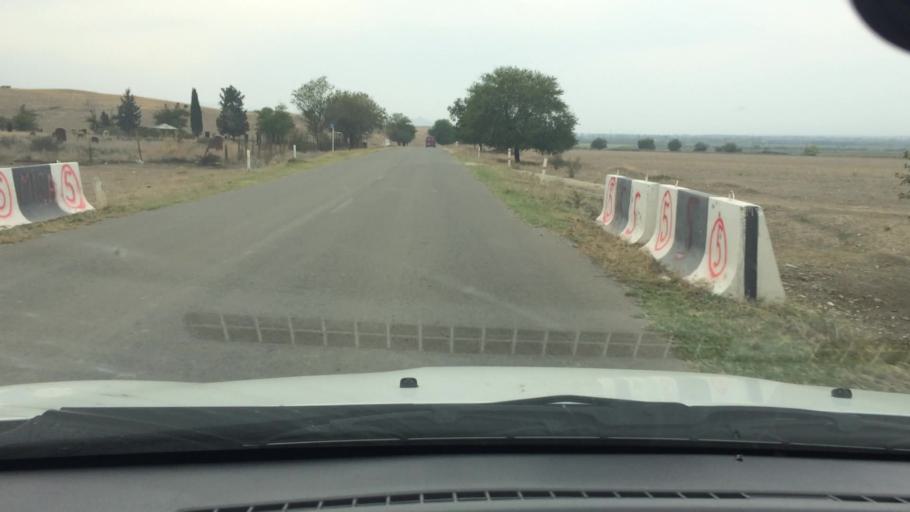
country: AM
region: Tavush
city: Berdavan
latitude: 41.3372
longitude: 45.0123
